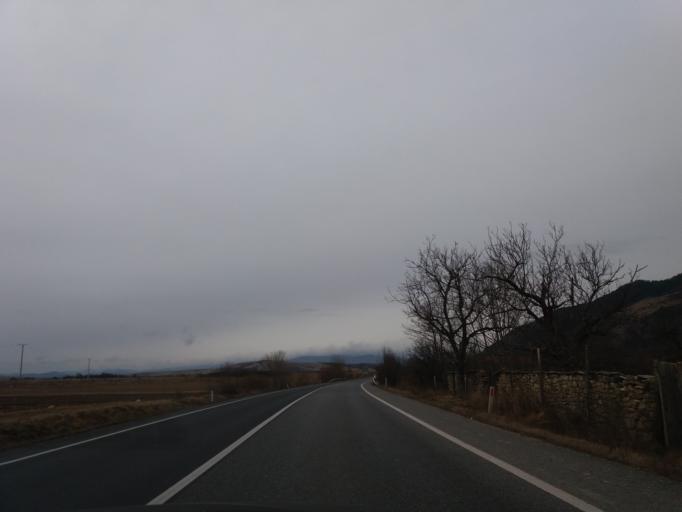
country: RO
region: Hunedoara
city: Salasu de Sus
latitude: 45.5336
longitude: 23.0107
